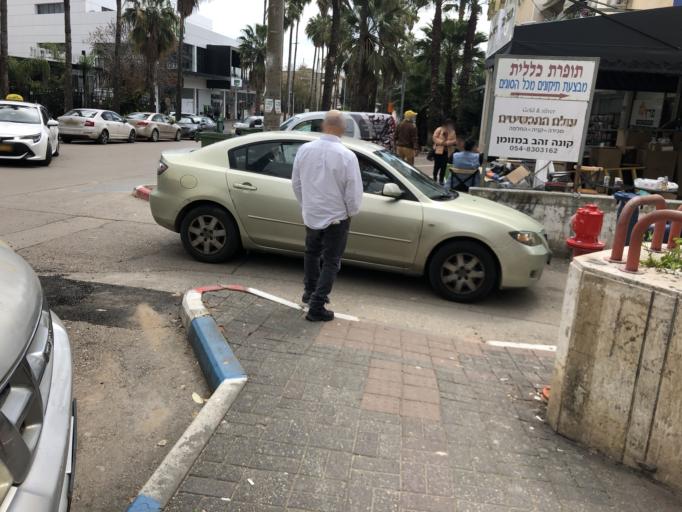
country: IL
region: Haifa
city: Hadera
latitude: 32.4737
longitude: 34.9734
